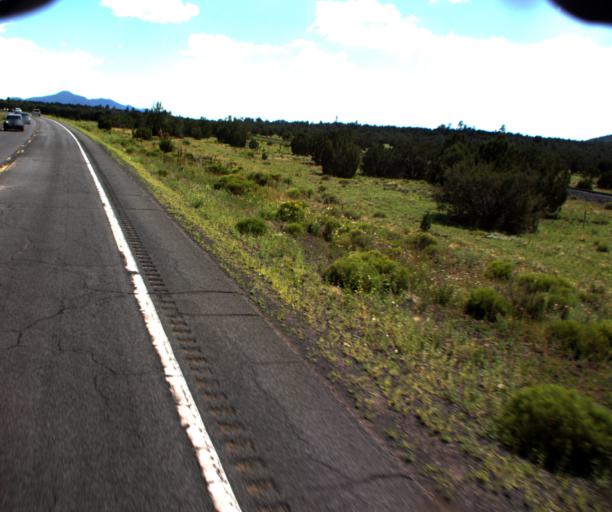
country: US
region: Arizona
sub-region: Coconino County
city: Williams
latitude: 35.3618
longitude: -112.1669
